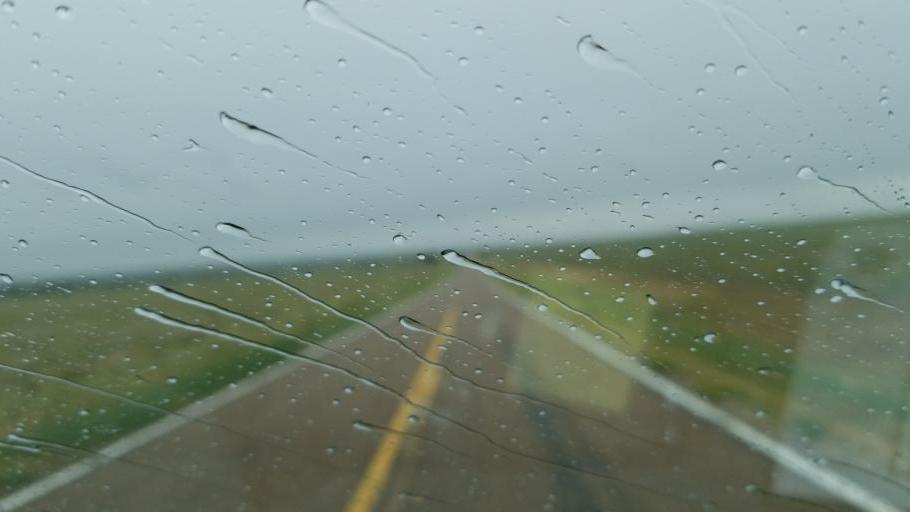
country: US
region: Colorado
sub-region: Lincoln County
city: Hugo
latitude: 38.8651
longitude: -103.1311
